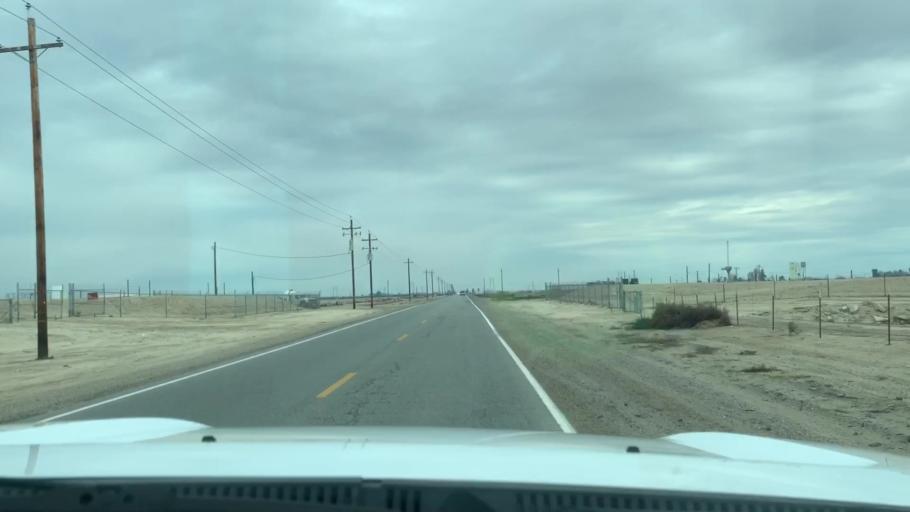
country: US
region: California
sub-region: Kern County
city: Rosedale
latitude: 35.3456
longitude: -119.2522
